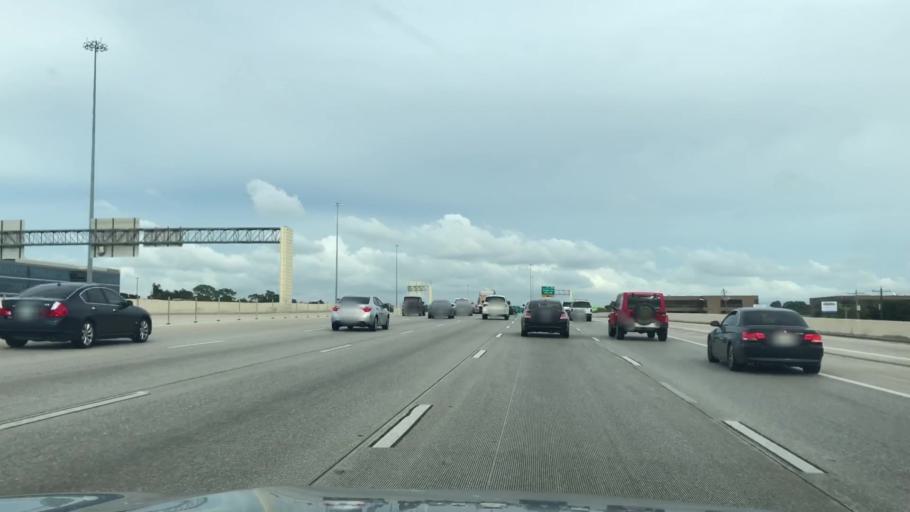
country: US
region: Texas
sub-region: Harris County
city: Hedwig Village
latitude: 29.7828
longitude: -95.5154
